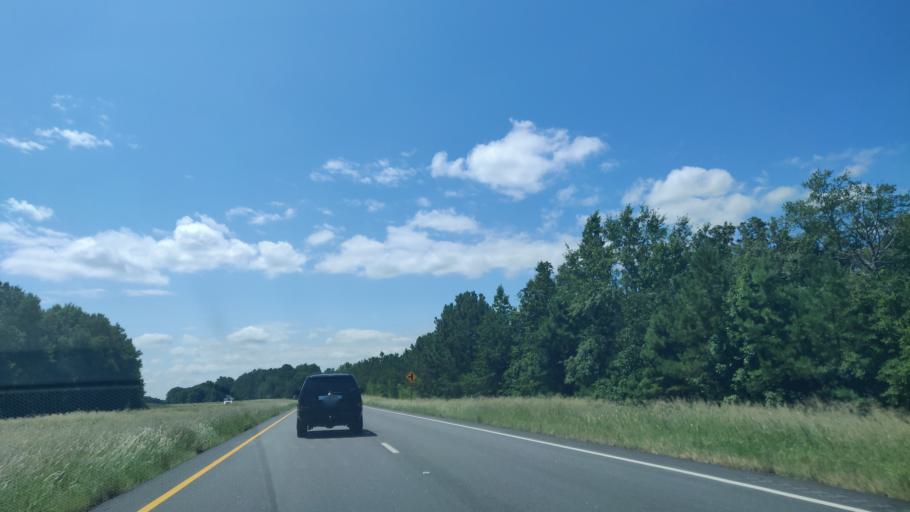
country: US
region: Georgia
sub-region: Stewart County
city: Richland
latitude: 32.1373
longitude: -84.6877
